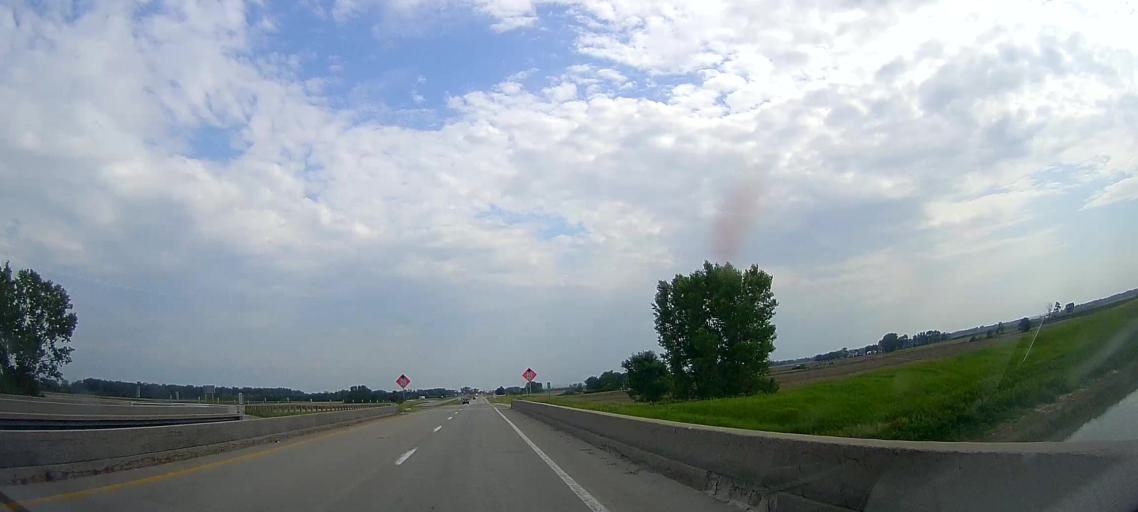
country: US
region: Nebraska
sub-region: Burt County
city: Tekamah
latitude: 41.7506
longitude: -96.0466
